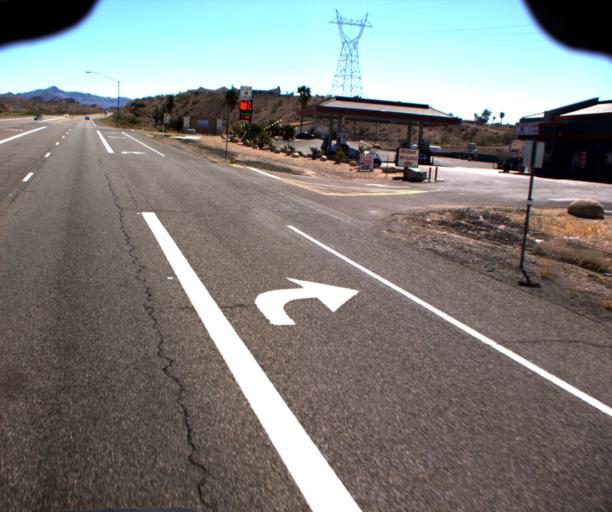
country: US
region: Nevada
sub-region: Clark County
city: Laughlin
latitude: 35.1905
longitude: -114.5286
